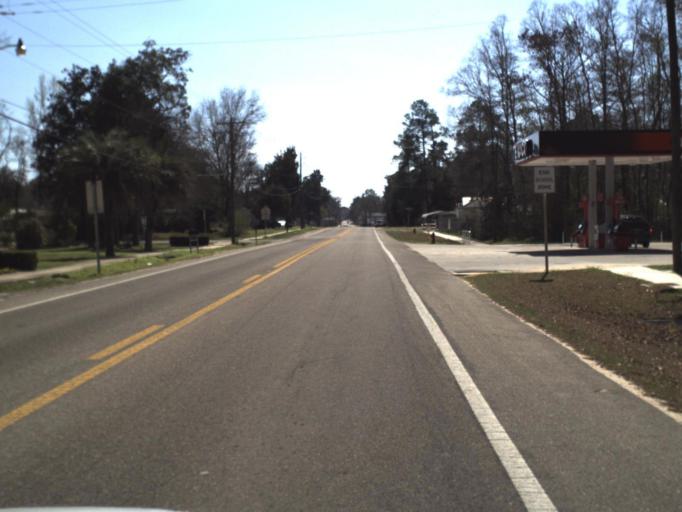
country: US
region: Florida
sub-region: Calhoun County
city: Blountstown
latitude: 30.4551
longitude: -85.0450
